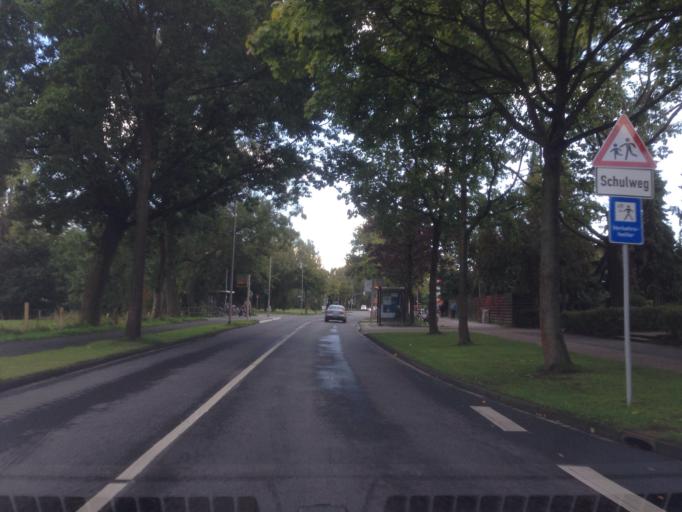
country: DE
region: North Rhine-Westphalia
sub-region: Regierungsbezirk Munster
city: Muenster
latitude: 51.9742
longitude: 7.5645
